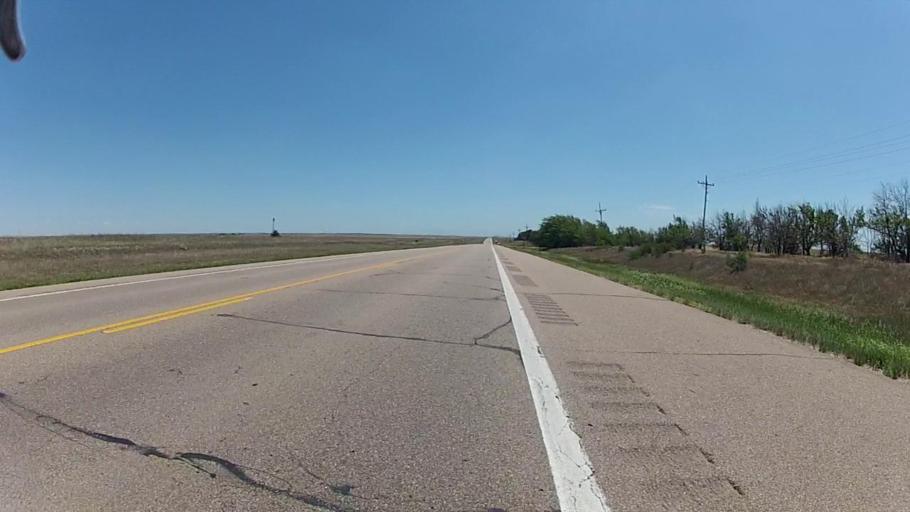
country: US
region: Kansas
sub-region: Ford County
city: Dodge City
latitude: 37.7083
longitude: -100.1259
